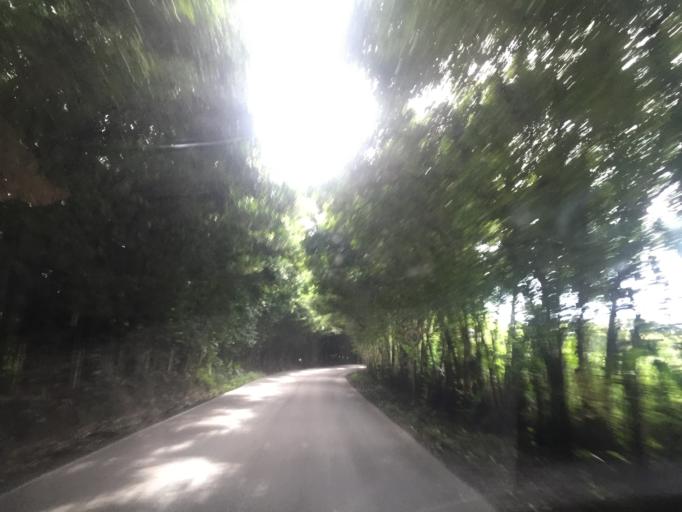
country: CO
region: Quindio
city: La Tebaida
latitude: 4.4721
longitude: -75.8175
